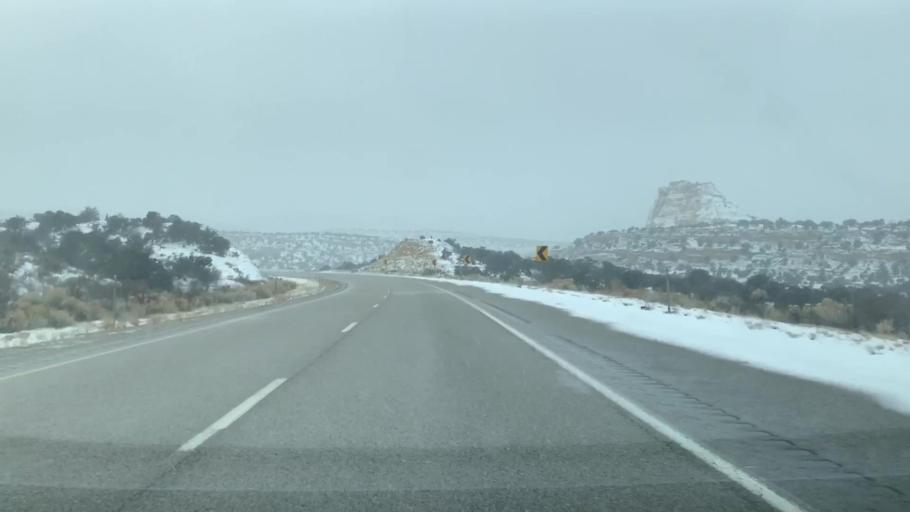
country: US
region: Utah
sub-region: Emery County
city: Ferron
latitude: 38.8628
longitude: -110.8618
